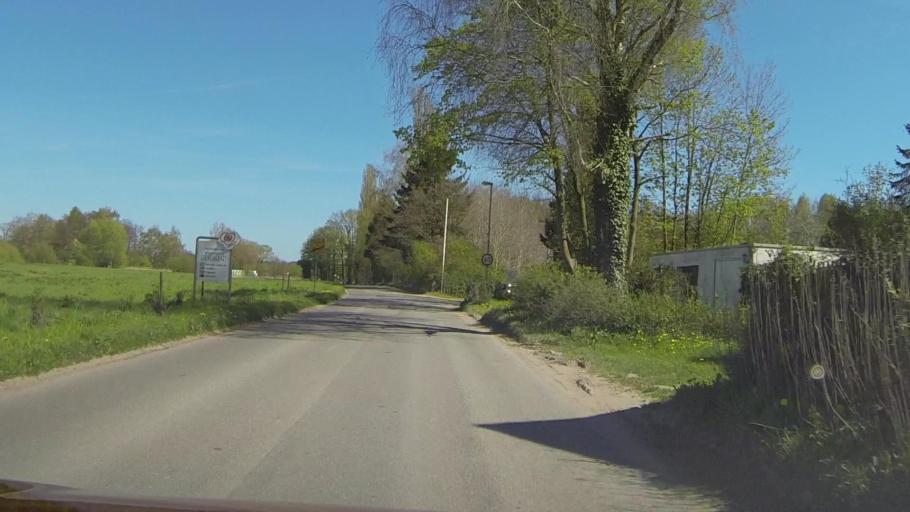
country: DE
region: Schleswig-Holstein
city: Tornesch
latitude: 53.6770
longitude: 9.6995
